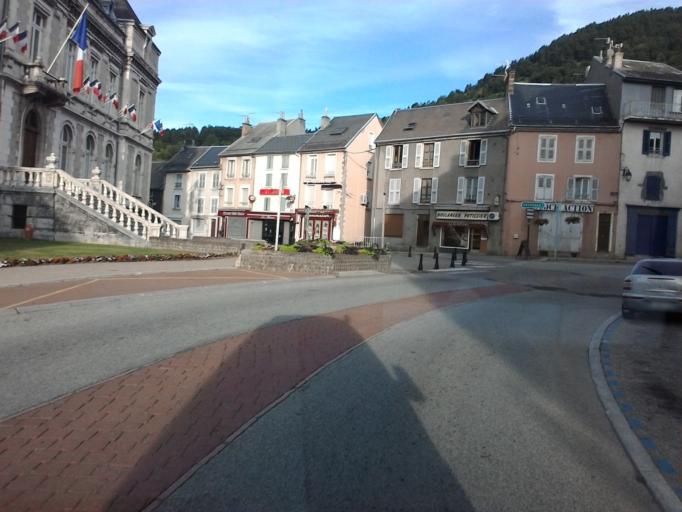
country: FR
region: Rhone-Alpes
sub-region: Departement de l'Isere
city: La Mure
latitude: 44.9068
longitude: 5.7849
